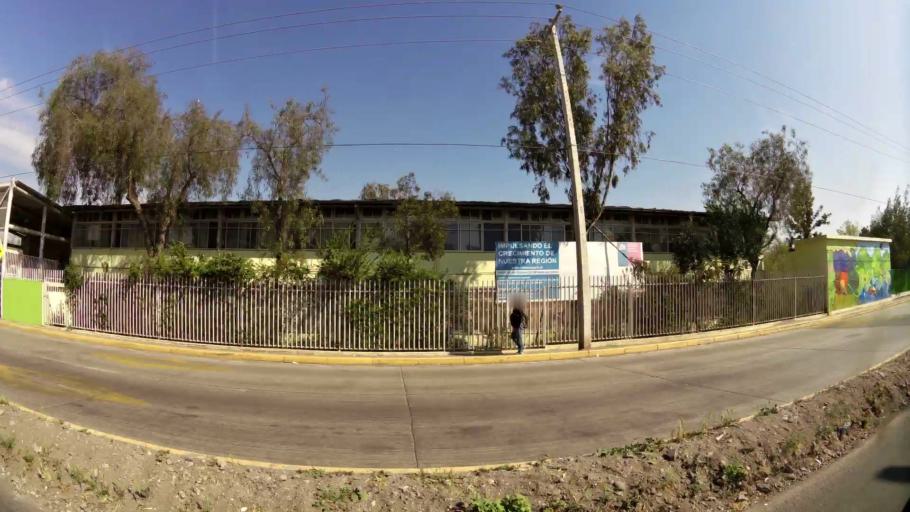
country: CL
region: Santiago Metropolitan
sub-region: Provincia de Maipo
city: San Bernardo
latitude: -33.5958
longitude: -70.6867
